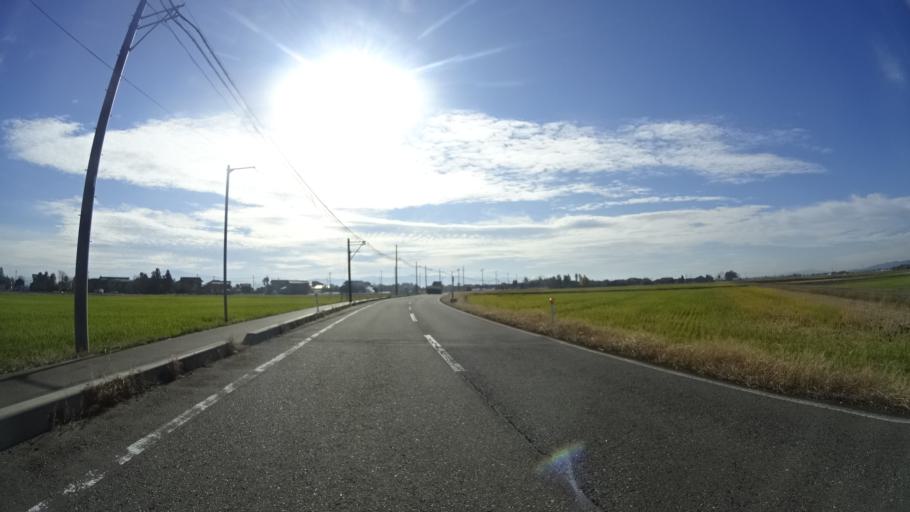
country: JP
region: Niigata
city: Mitsuke
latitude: 37.5633
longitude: 138.8488
